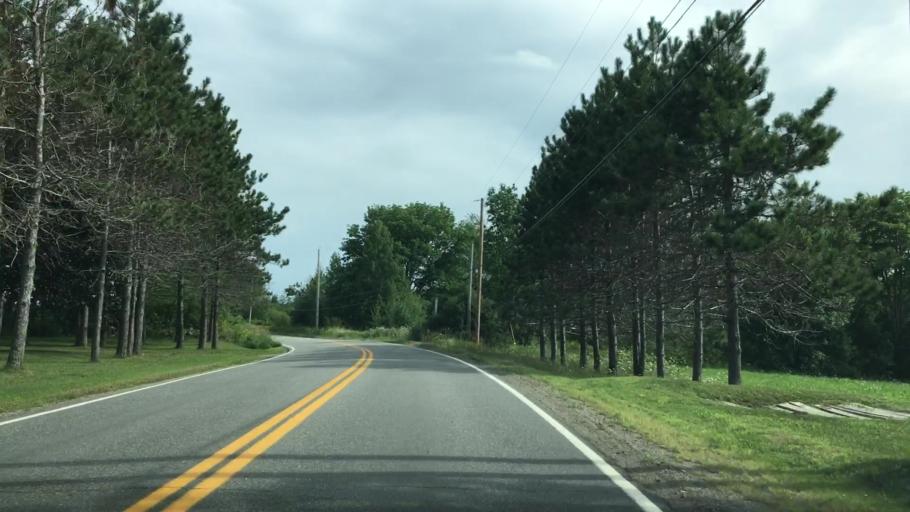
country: US
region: Maine
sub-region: Waldo County
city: Belfast
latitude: 44.3789
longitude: -69.0341
